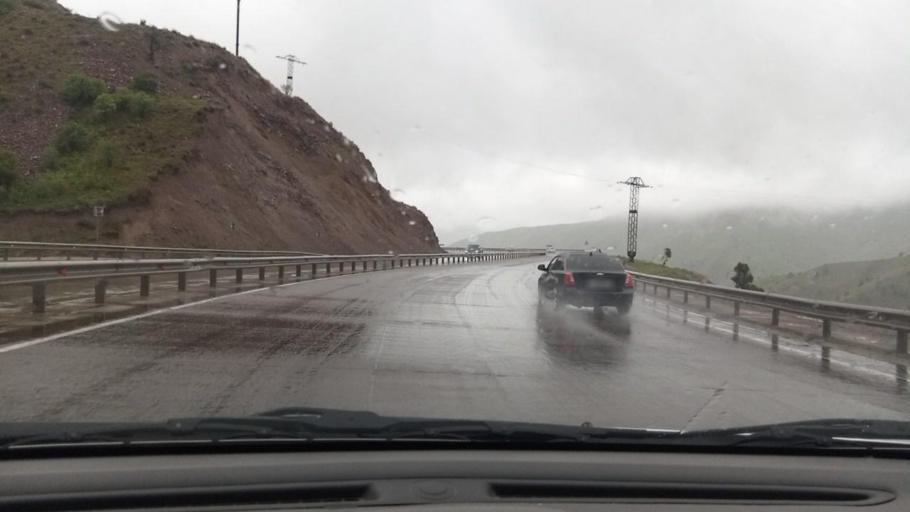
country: UZ
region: Toshkent
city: Angren
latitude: 41.0894
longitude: 70.5355
